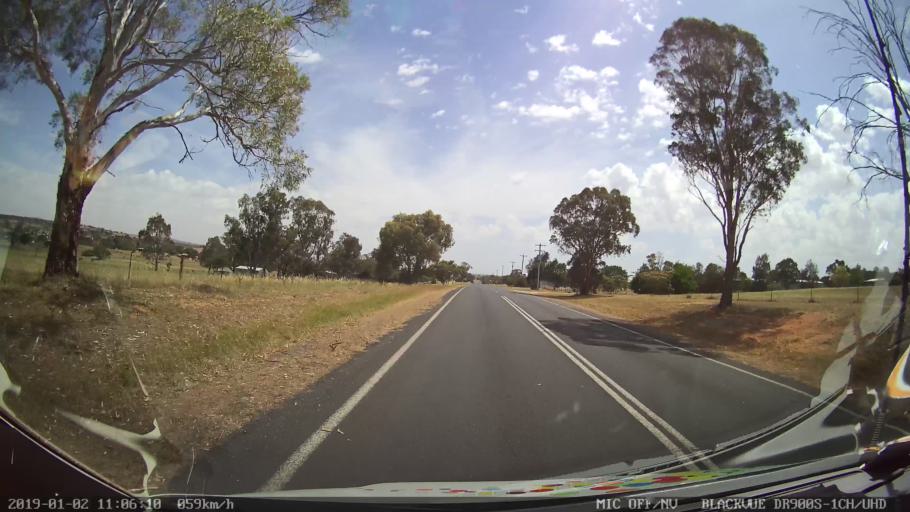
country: AU
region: New South Wales
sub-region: Young
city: Young
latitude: -34.5572
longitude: 148.3557
